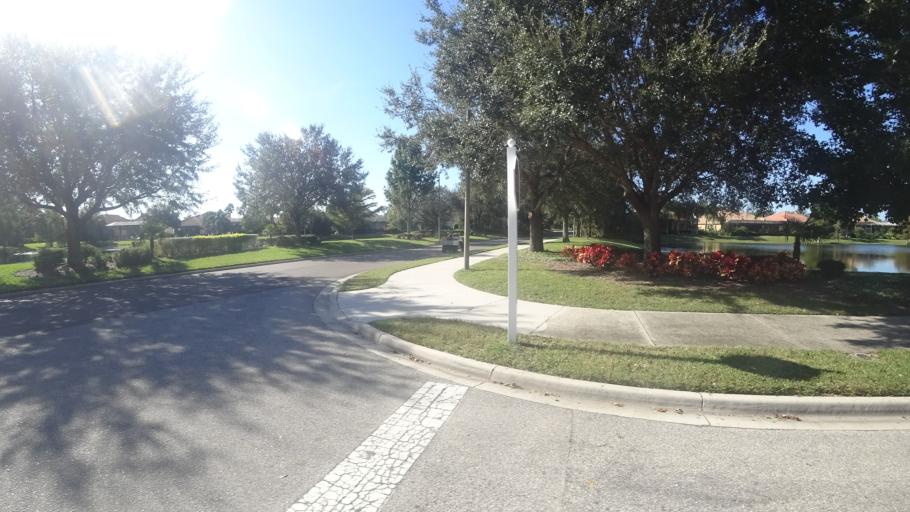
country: US
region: Florida
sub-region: Sarasota County
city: The Meadows
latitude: 27.4025
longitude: -82.4045
